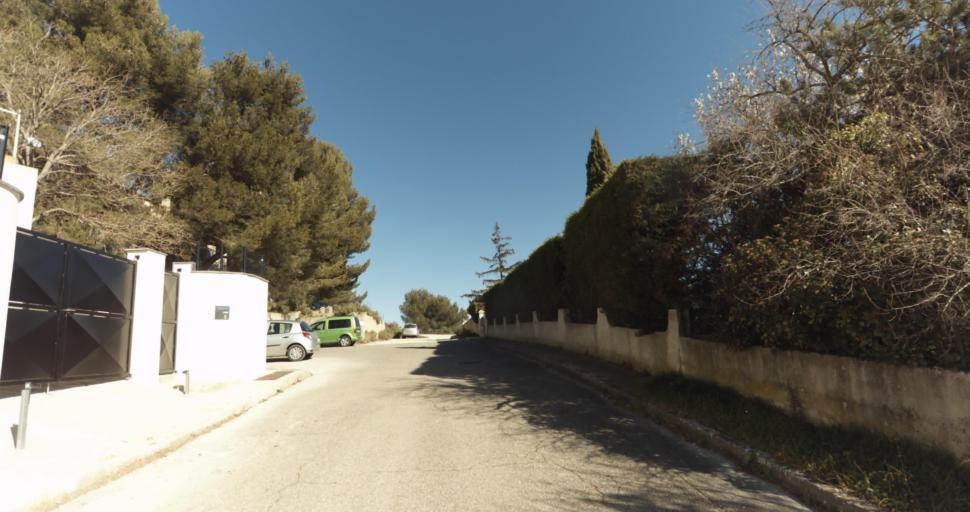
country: FR
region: Provence-Alpes-Cote d'Azur
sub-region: Departement des Bouches-du-Rhone
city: Peypin
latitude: 43.3864
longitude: 5.5651
